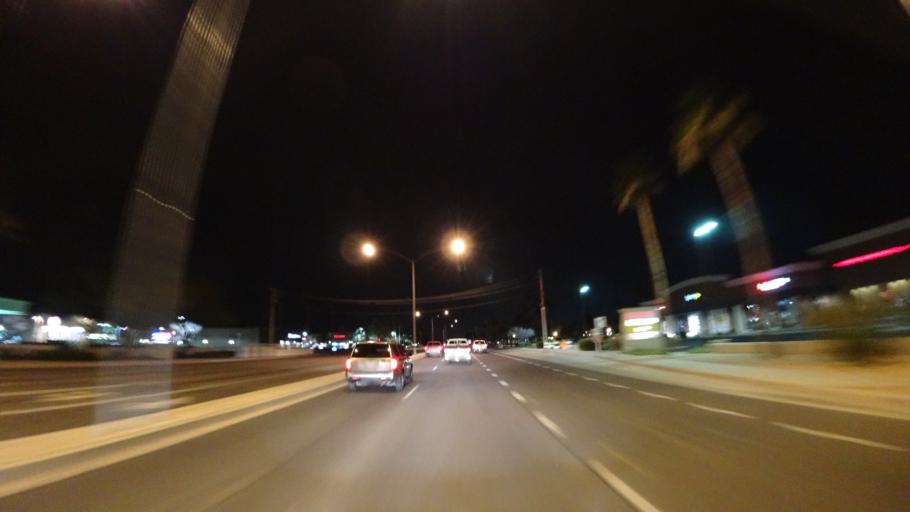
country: US
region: Arizona
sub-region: Maricopa County
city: Gilbert
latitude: 33.3795
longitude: -111.6881
